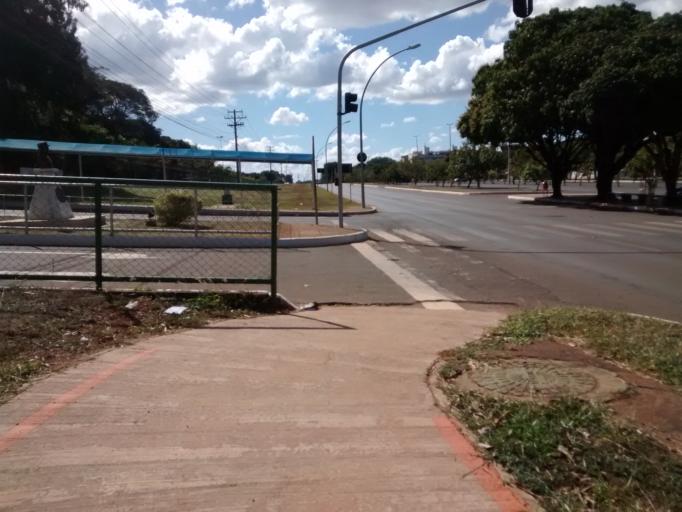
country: BR
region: Federal District
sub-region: Brasilia
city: Brasilia
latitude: -15.7807
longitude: -47.8913
